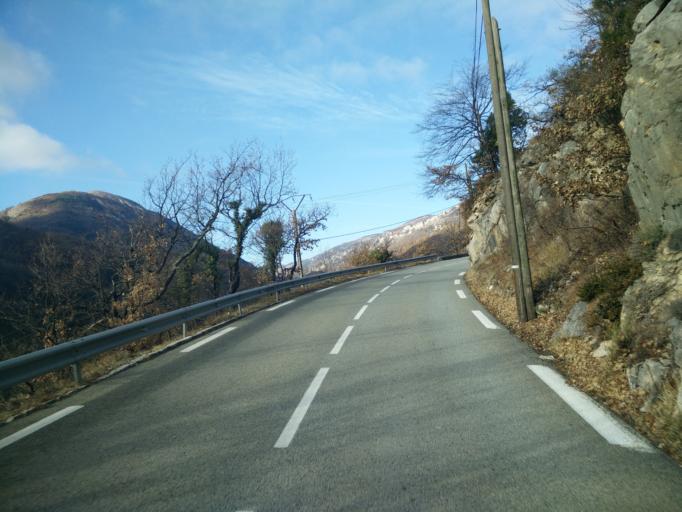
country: FR
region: Provence-Alpes-Cote d'Azur
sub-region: Departement des Alpes-Maritimes
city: Tourrettes-sur-Loup
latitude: 43.7886
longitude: 6.9716
